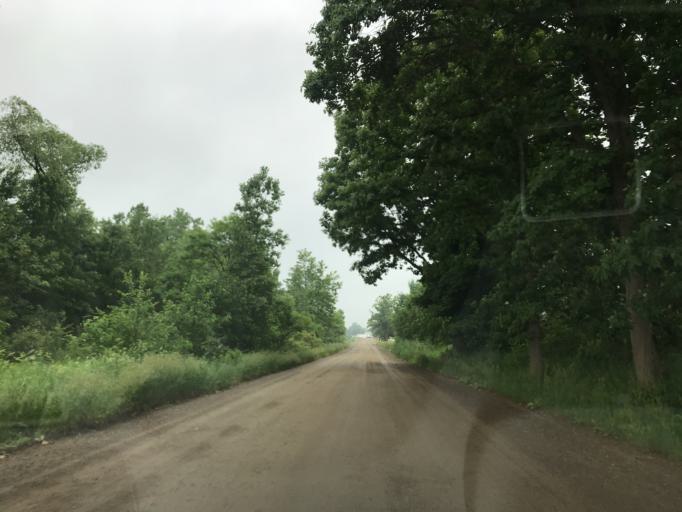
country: US
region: Michigan
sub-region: Oakland County
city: Wixom
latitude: 42.5022
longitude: -83.5954
